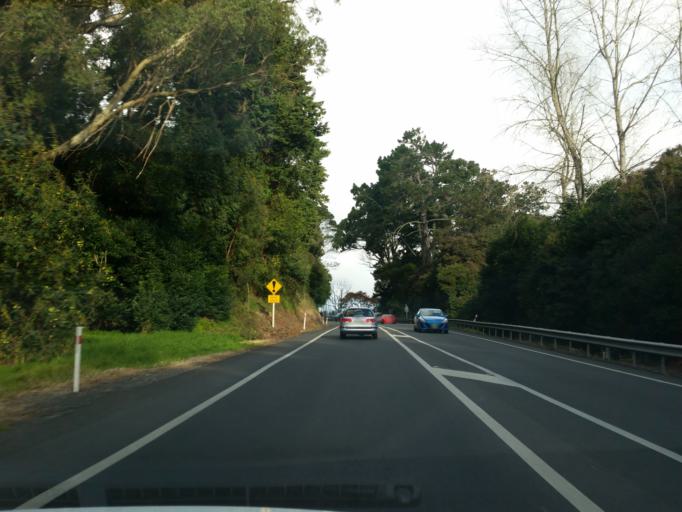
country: NZ
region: Bay of Plenty
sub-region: Tauranga City
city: Tauranga
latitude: -37.6985
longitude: 176.0774
